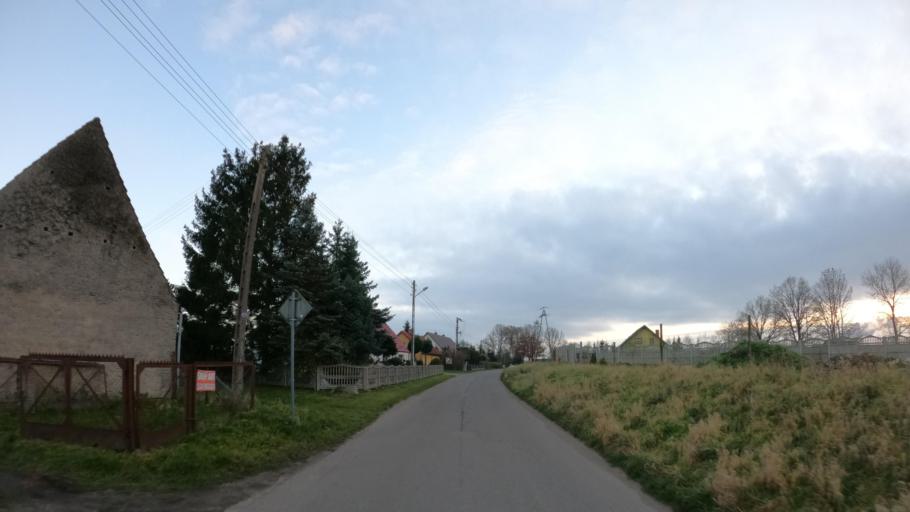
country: PL
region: West Pomeranian Voivodeship
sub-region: Powiat bialogardzki
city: Karlino
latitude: 54.0768
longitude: 15.8826
